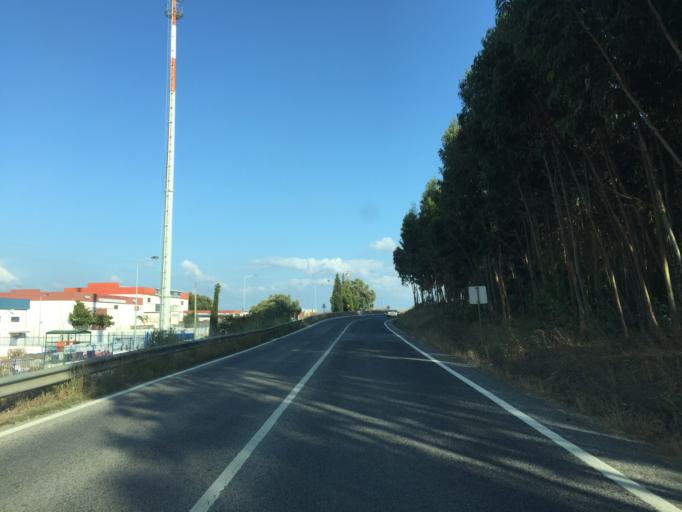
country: PT
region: Lisbon
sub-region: Alenquer
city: Alenquer
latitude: 39.1284
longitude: -8.9926
